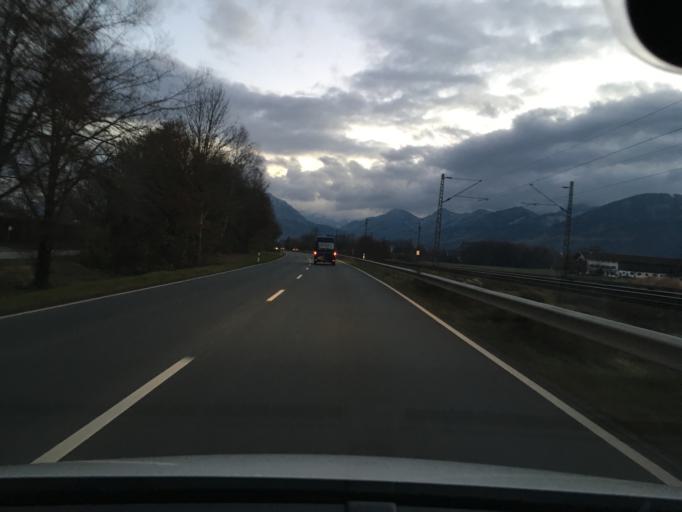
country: DE
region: Bavaria
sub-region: Upper Bavaria
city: Raubling
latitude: 47.7808
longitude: 12.1053
